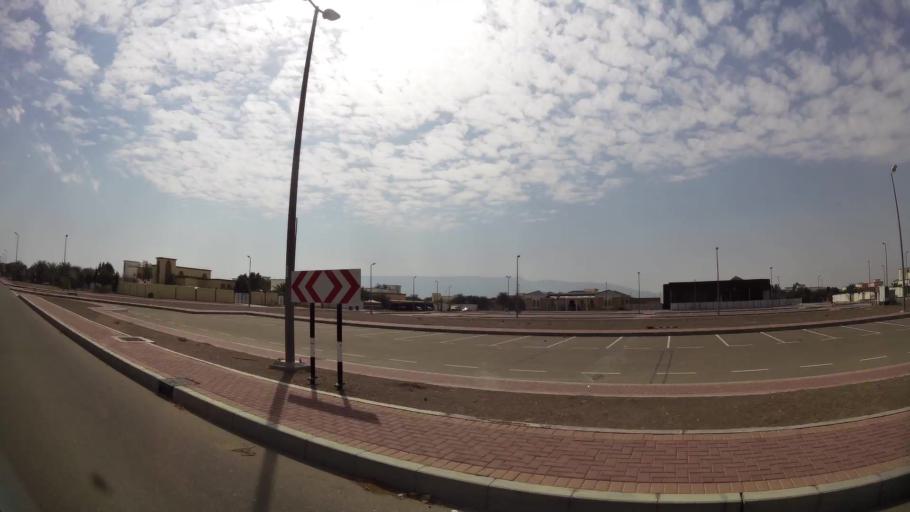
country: AE
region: Abu Dhabi
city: Al Ain
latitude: 24.0987
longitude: 55.8930
